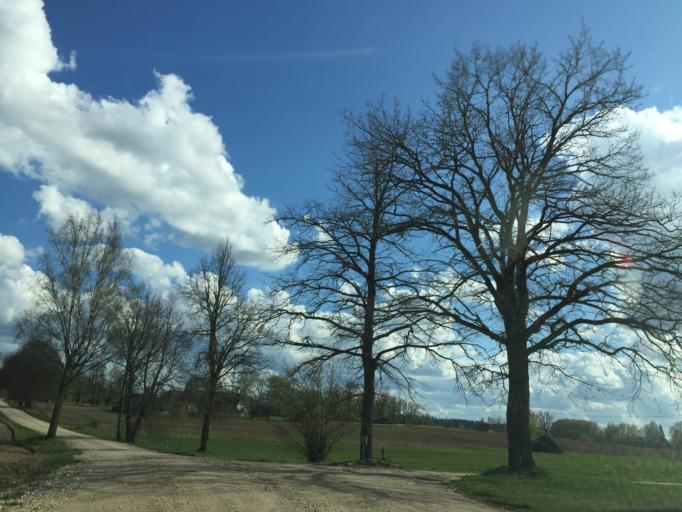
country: LV
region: Beverina
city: Murmuiza
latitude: 57.4211
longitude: 25.5499
